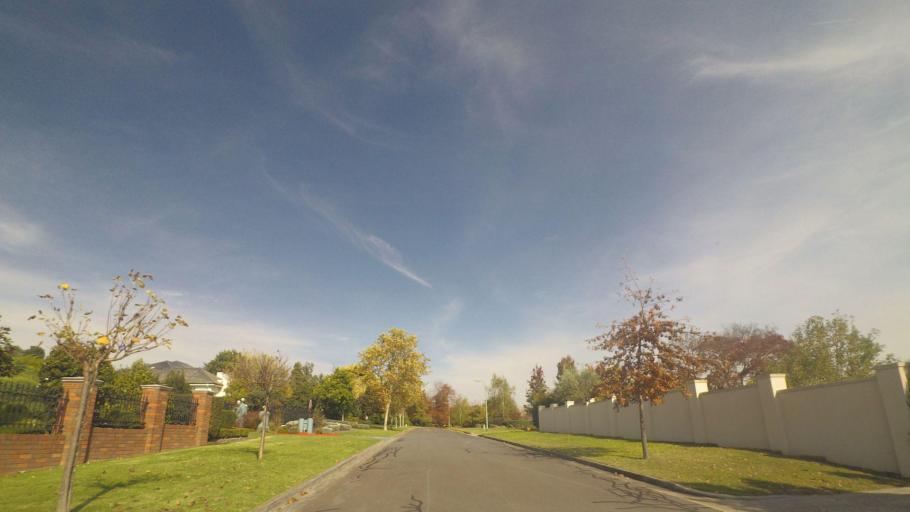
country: AU
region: Victoria
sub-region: Manningham
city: Doncaster East
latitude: -37.7629
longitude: 145.1468
